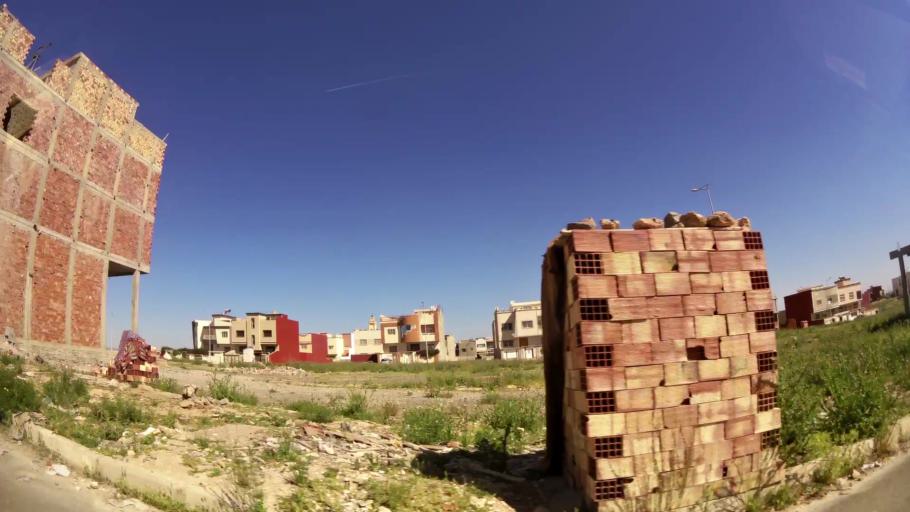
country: MA
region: Oriental
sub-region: Oujda-Angad
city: Oujda
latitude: 34.6529
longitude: -1.8851
